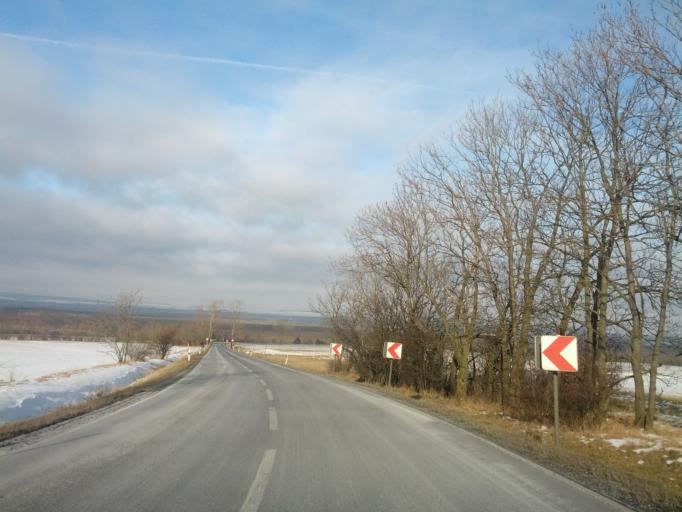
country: DE
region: Thuringia
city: Schonstedt
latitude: 51.0713
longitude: 10.5931
